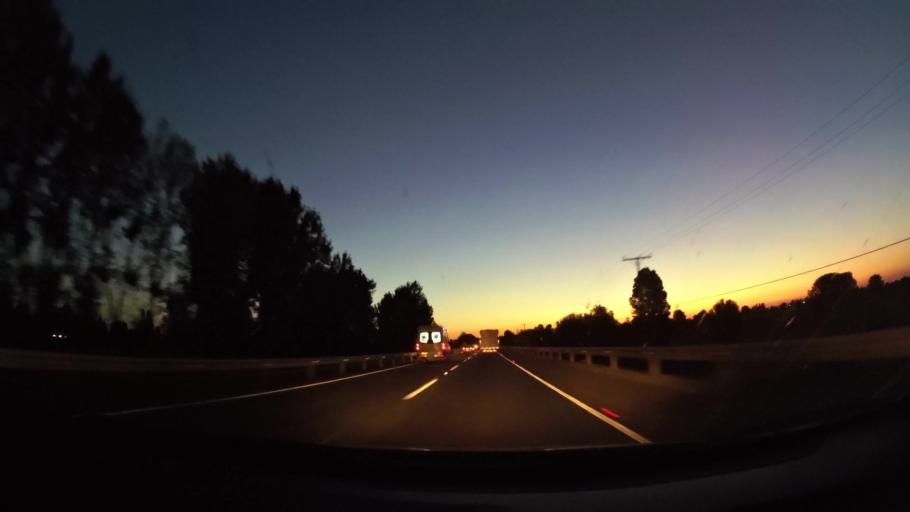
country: CL
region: Biobio
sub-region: Provincia de Nuble
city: San Carlos
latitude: -36.3816
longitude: -71.9099
